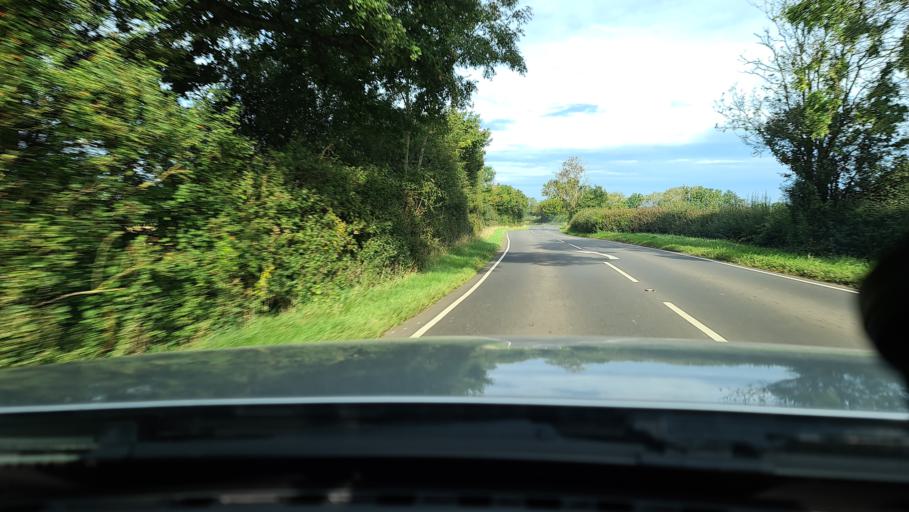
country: GB
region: England
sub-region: Warwickshire
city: Wellesbourne Mountford
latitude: 52.1181
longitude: -1.4959
